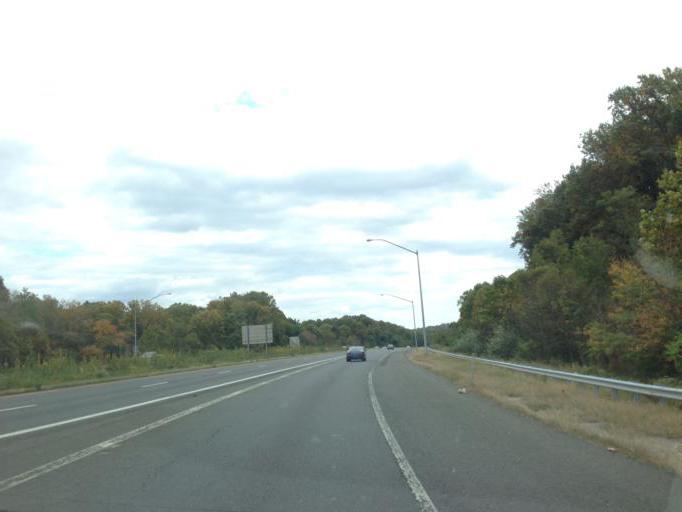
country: US
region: Maryland
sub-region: Howard County
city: Highland
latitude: 39.2058
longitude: -76.9383
